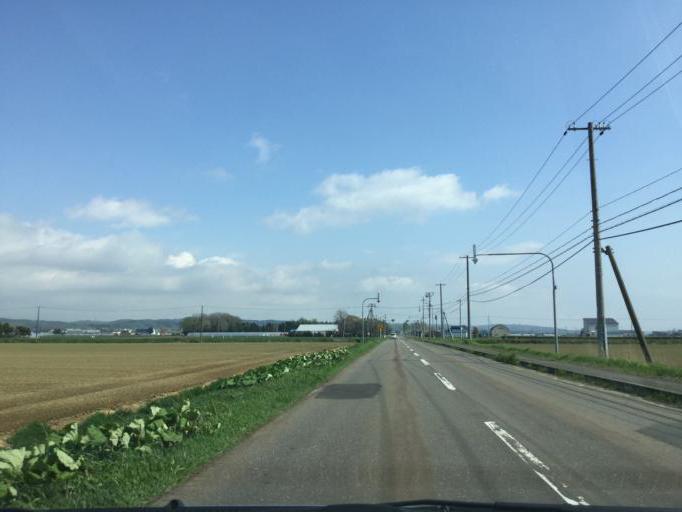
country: JP
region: Hokkaido
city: Iwamizawa
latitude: 43.1440
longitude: 141.7224
